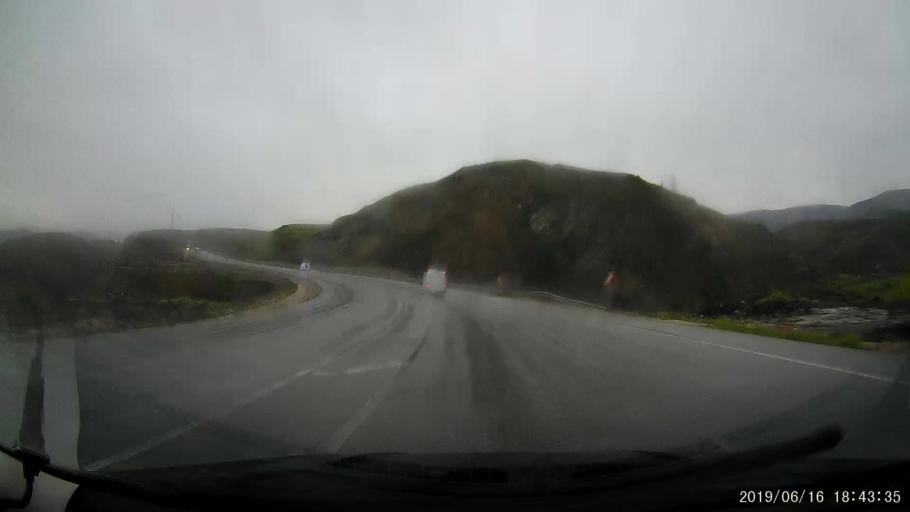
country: TR
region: Erzincan
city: Doganbeyli
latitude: 39.8714
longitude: 39.0904
